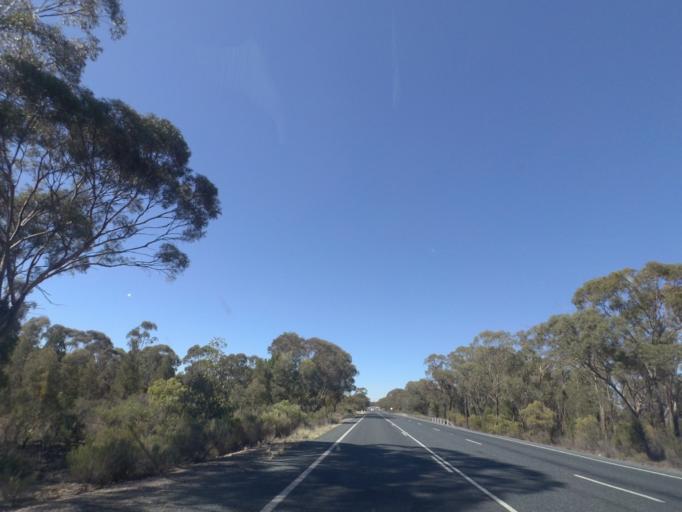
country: AU
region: New South Wales
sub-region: Bland
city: West Wyalong
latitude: -34.1315
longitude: 147.1233
